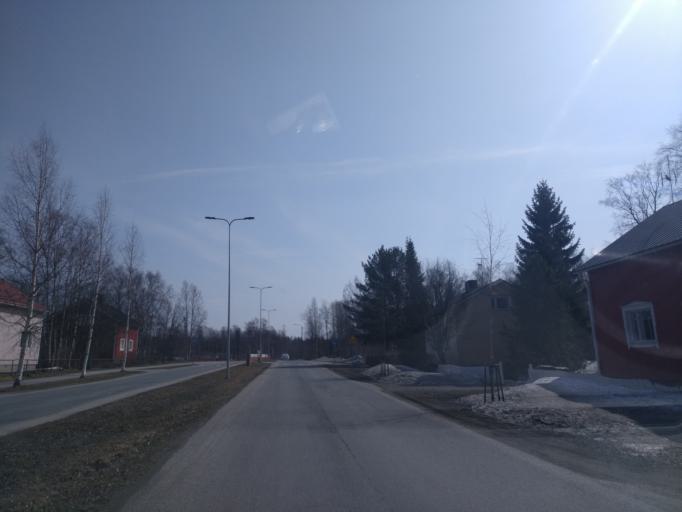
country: FI
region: Lapland
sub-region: Kemi-Tornio
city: Kemi
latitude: 65.7282
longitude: 24.6110
